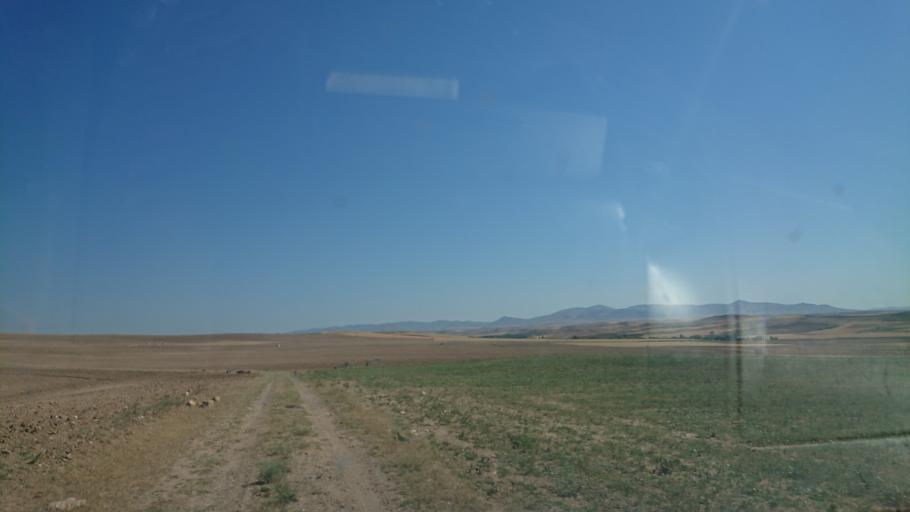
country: TR
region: Aksaray
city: Sariyahsi
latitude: 39.0487
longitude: 33.8903
